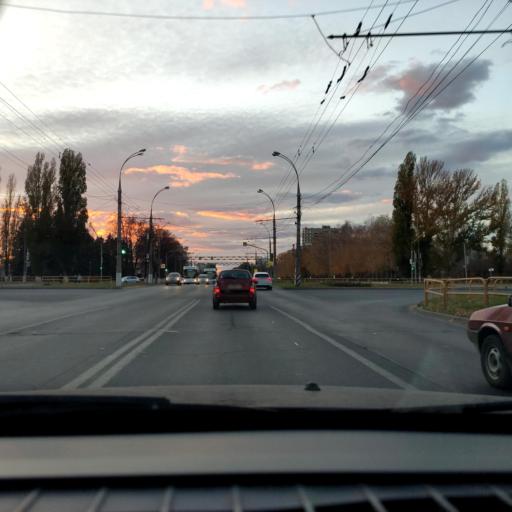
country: RU
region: Samara
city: Tol'yatti
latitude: 53.5057
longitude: 49.2766
